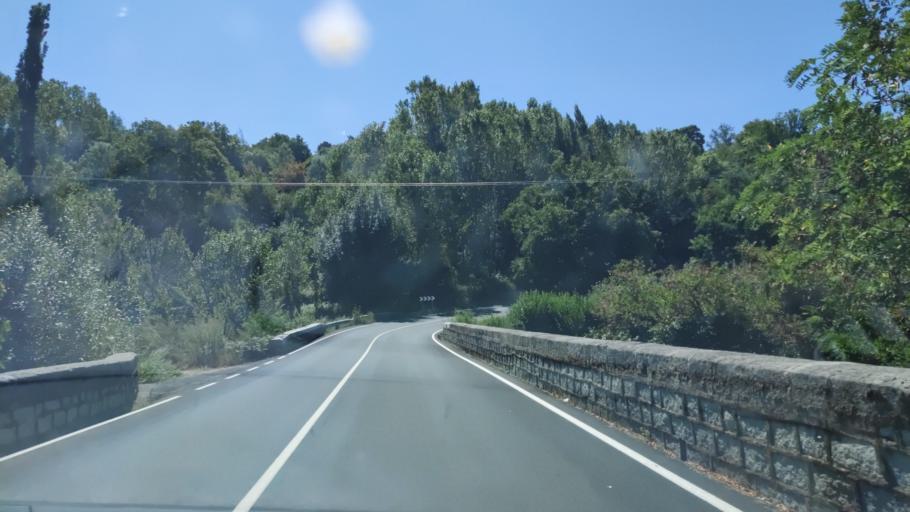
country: ES
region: Castille and Leon
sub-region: Provincia de Salamanca
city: Candelario
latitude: 40.3707
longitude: -5.7518
